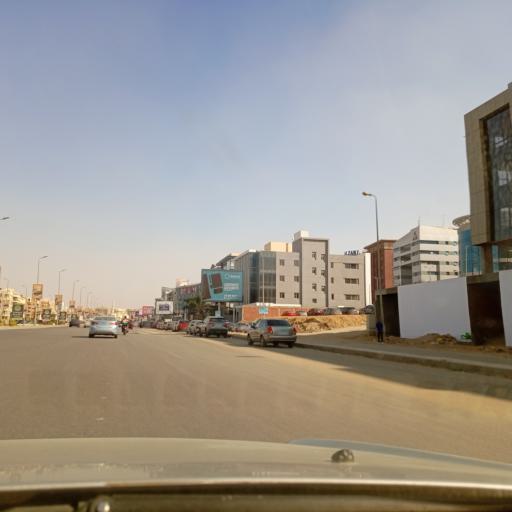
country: EG
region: Muhafazat al Qalyubiyah
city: Al Khankah
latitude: 30.0302
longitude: 31.4582
